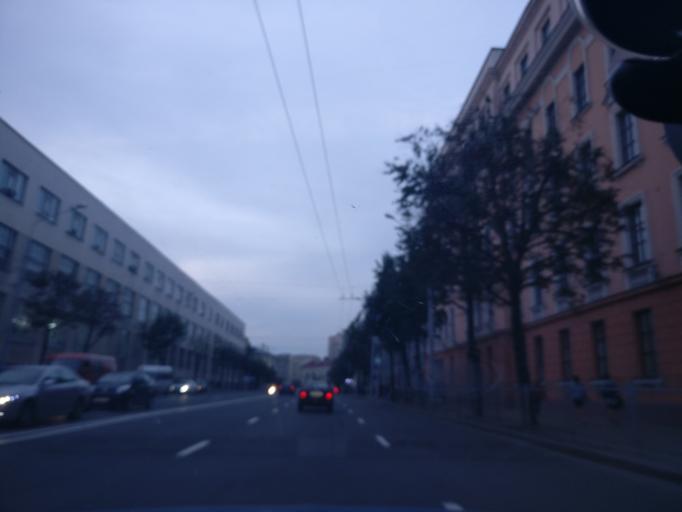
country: BY
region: Minsk
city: Minsk
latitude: 53.9226
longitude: 27.6009
